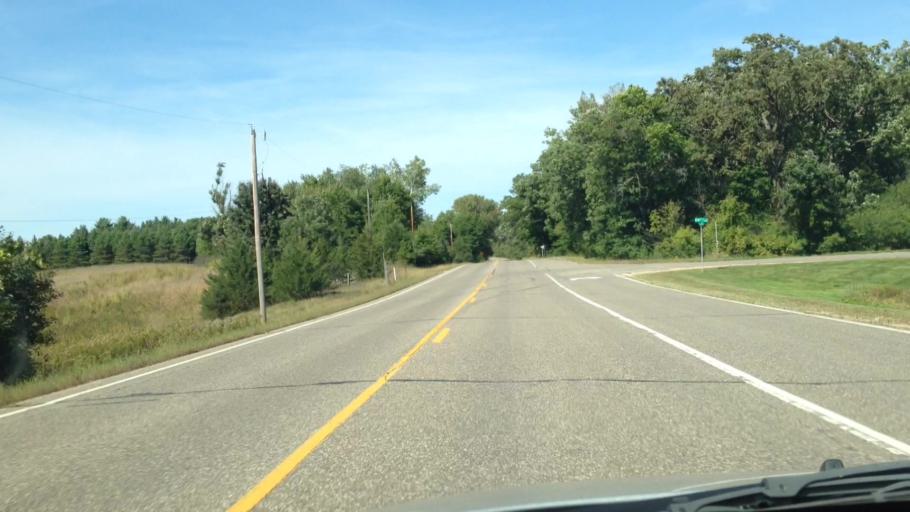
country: US
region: Minnesota
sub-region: Washington County
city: Stillwater
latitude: 45.1126
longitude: -92.8128
